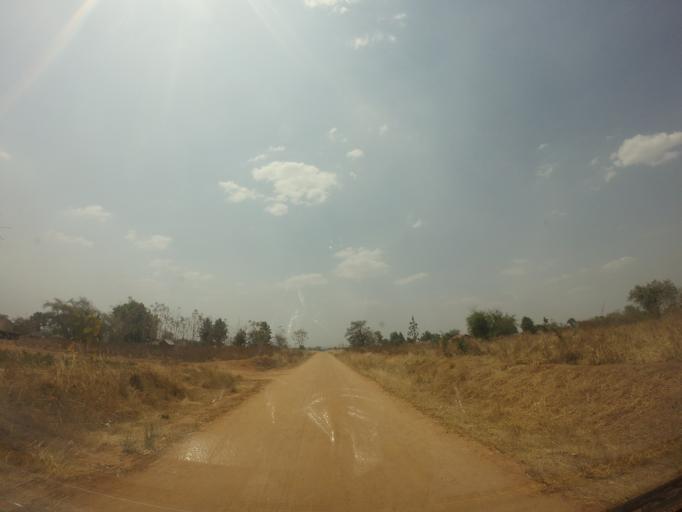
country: UG
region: Northern Region
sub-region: Arua District
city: Arua
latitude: 2.8836
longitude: 31.2113
